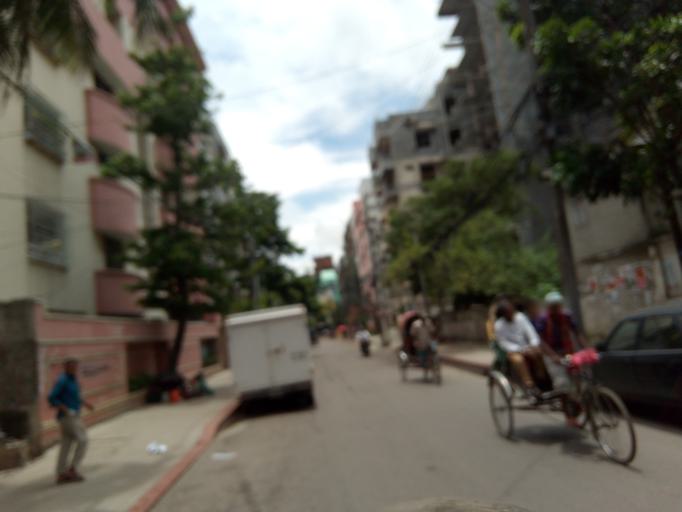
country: BD
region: Dhaka
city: Azimpur
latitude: 23.7429
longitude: 90.3749
